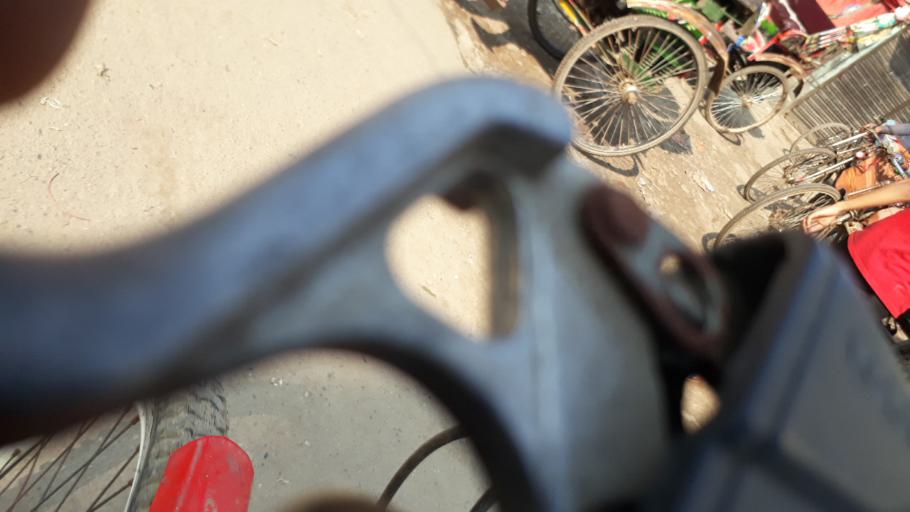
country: BD
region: Dhaka
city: Tungi
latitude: 23.8467
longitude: 90.2460
